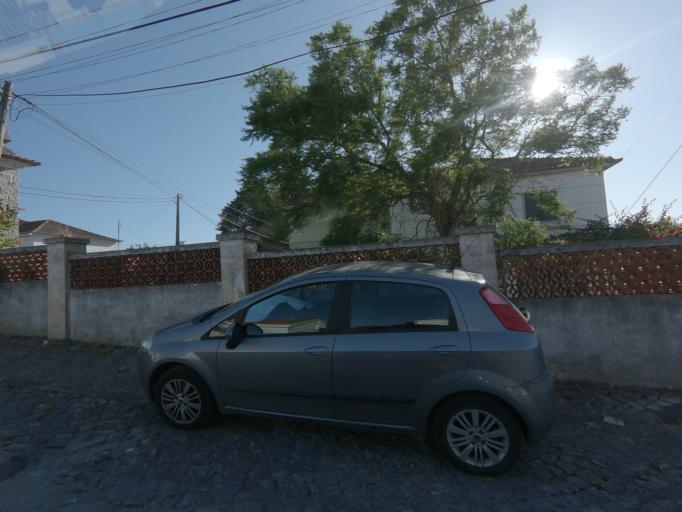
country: PT
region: Setubal
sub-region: Palmela
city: Palmela
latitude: 38.5785
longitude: -8.9082
